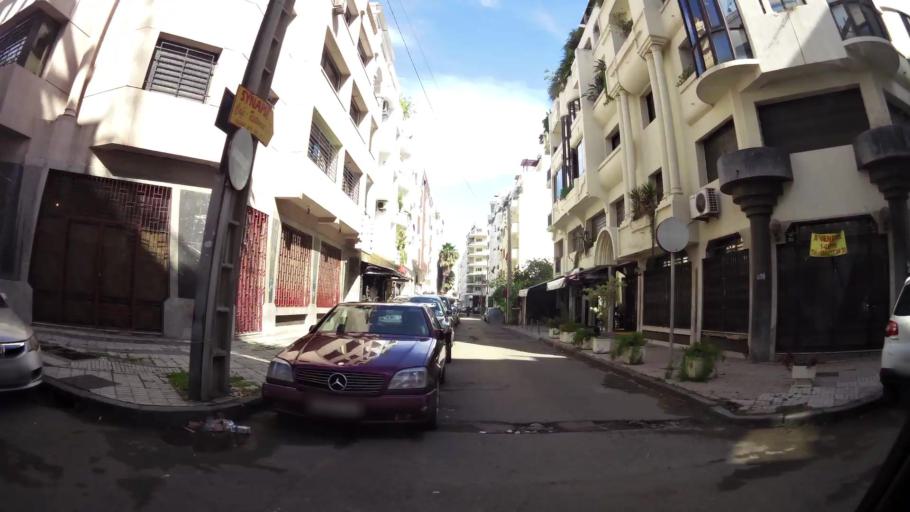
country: MA
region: Grand Casablanca
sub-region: Casablanca
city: Casablanca
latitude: 33.5890
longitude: -7.6357
